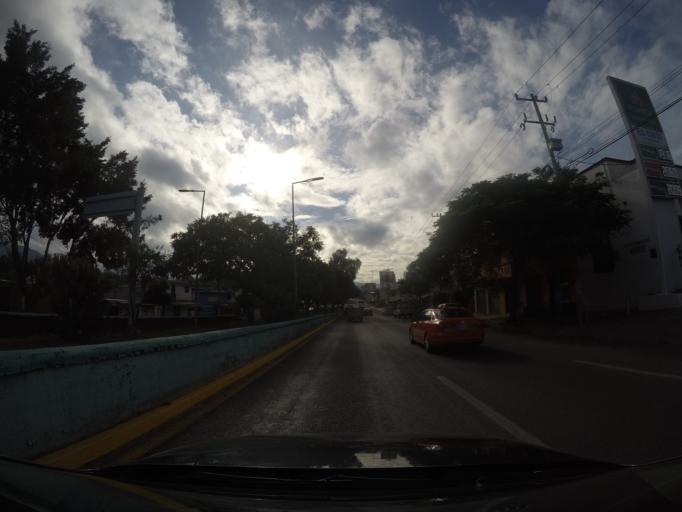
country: MX
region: Oaxaca
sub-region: Santa Cruz Amilpas
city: Santa Cruz Amilpas
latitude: 17.0693
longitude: -96.7016
